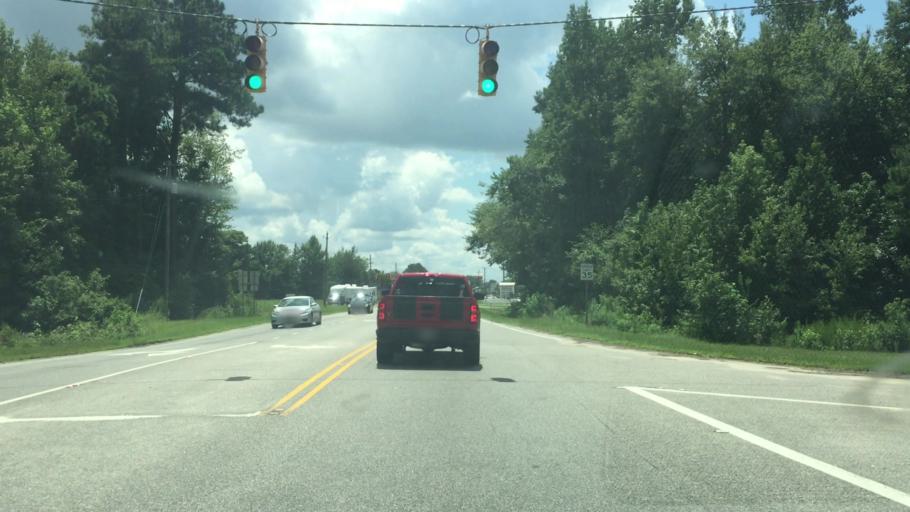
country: US
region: North Carolina
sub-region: Columbus County
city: Chadbourn
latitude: 34.3357
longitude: -78.8270
